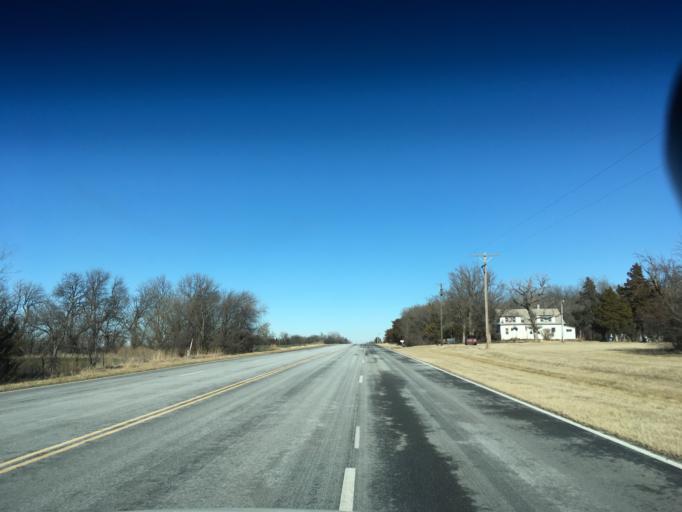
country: US
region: Kansas
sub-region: Harvey County
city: Sedgwick
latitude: 37.9220
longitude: -97.3364
